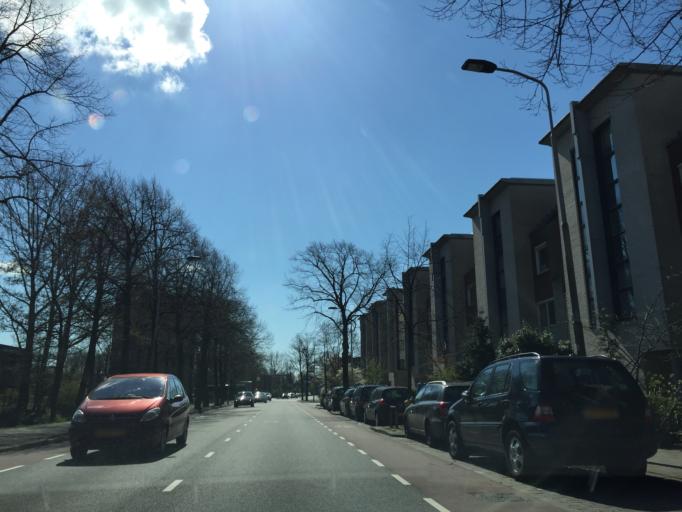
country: NL
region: South Holland
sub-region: Gemeente Delft
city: Delft
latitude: 52.0161
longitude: 4.3652
